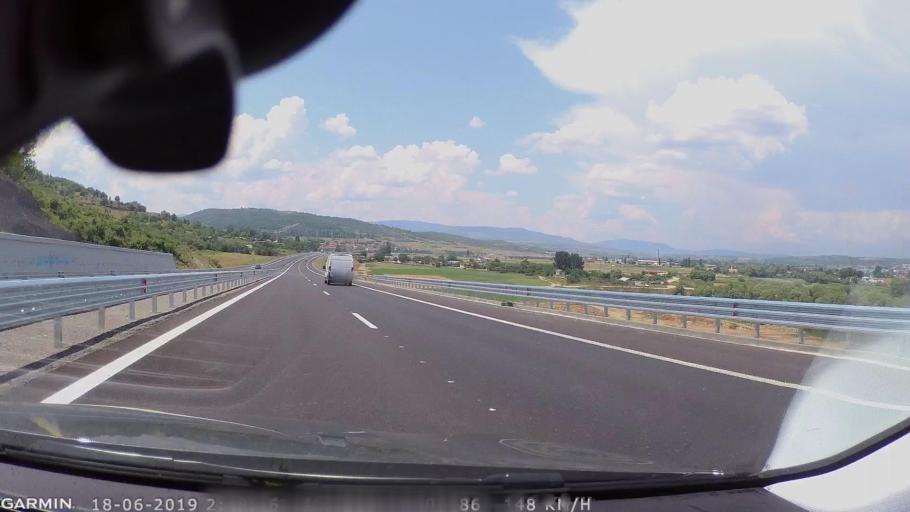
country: BG
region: Blagoevgrad
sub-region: Obshtina Blagoevgrad
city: Blagoevgrad
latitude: 41.9734
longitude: 23.0782
